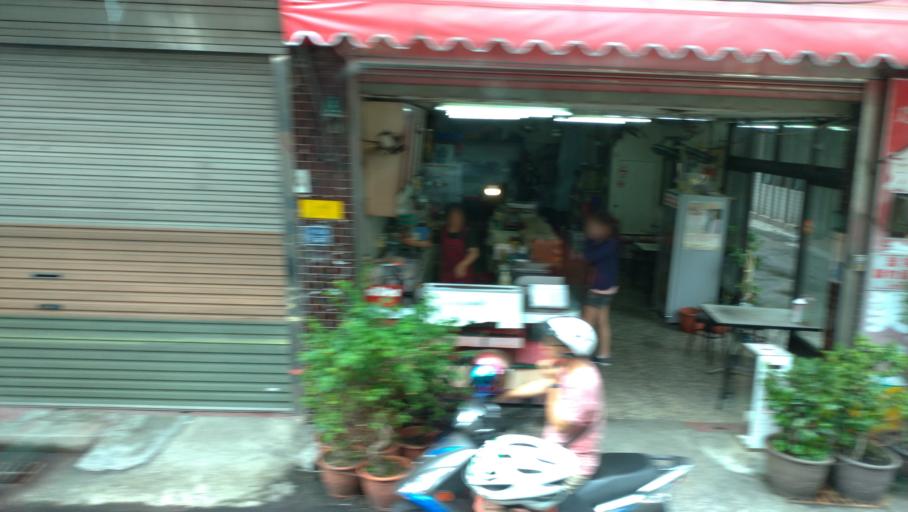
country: TW
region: Taiwan
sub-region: Keelung
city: Keelung
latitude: 25.1427
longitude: 121.7609
